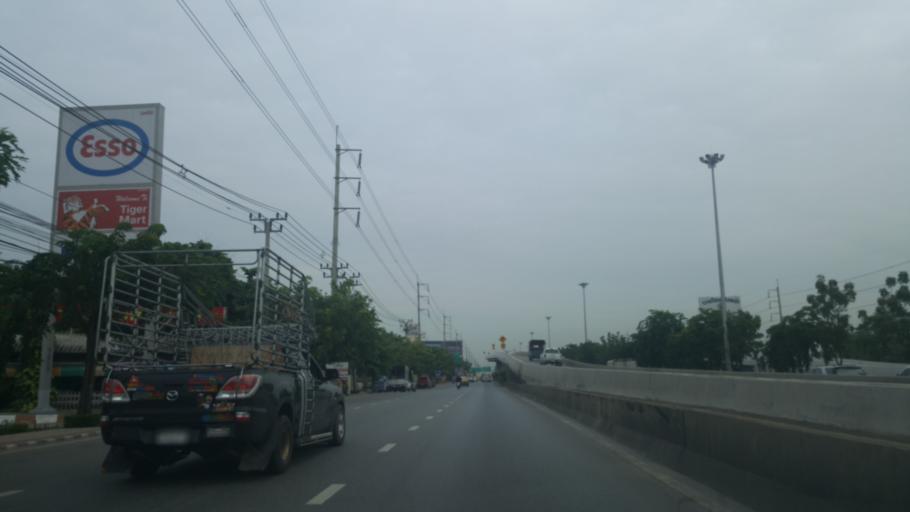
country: TH
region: Bangkok
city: Bang Bon
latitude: 13.6725
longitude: 100.4059
